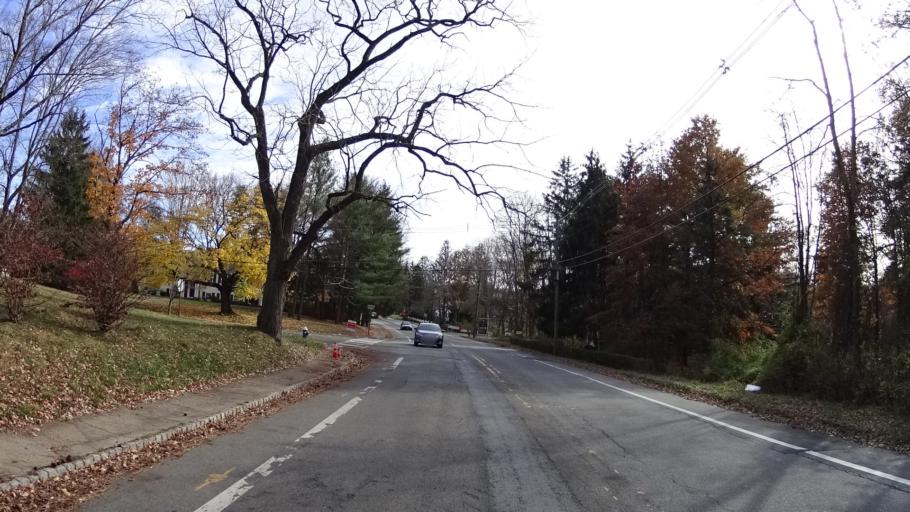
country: US
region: New Jersey
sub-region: Morris County
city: Madison
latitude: 40.7325
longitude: -74.4185
